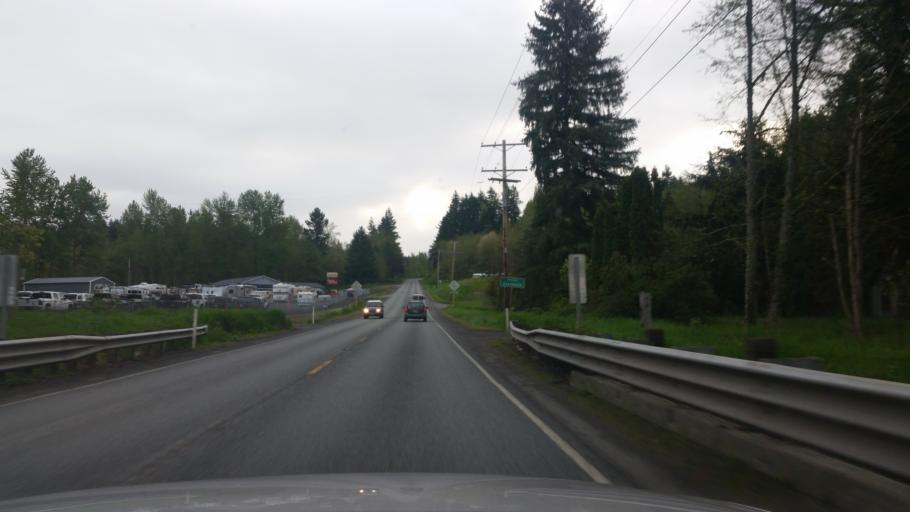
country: US
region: Washington
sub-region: Pierce County
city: Eatonville
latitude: 46.8738
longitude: -122.2685
